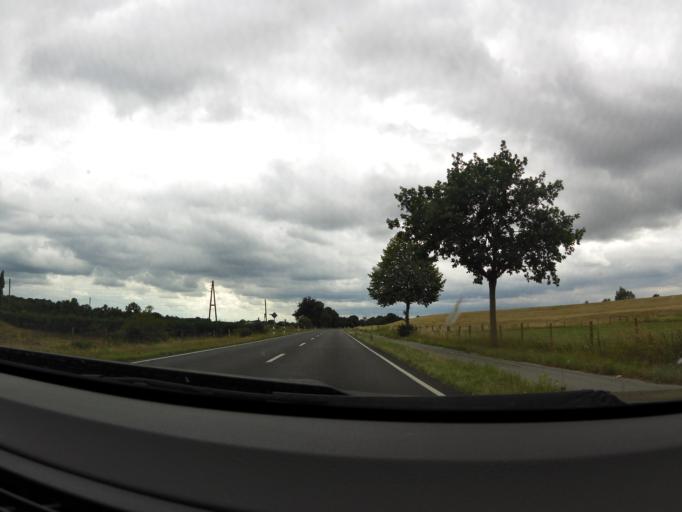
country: DE
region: North Rhine-Westphalia
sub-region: Regierungsbezirk Dusseldorf
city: Alpen
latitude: 51.6328
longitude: 6.5118
